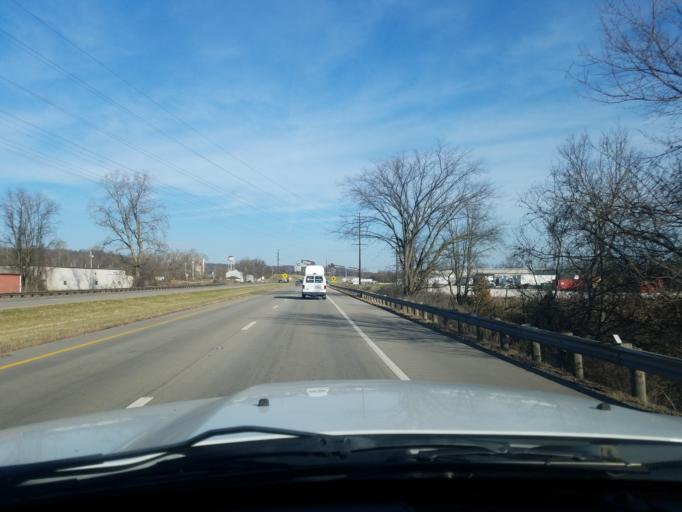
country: US
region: West Virginia
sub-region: Wood County
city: Vienna
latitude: 39.3625
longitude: -81.5390
